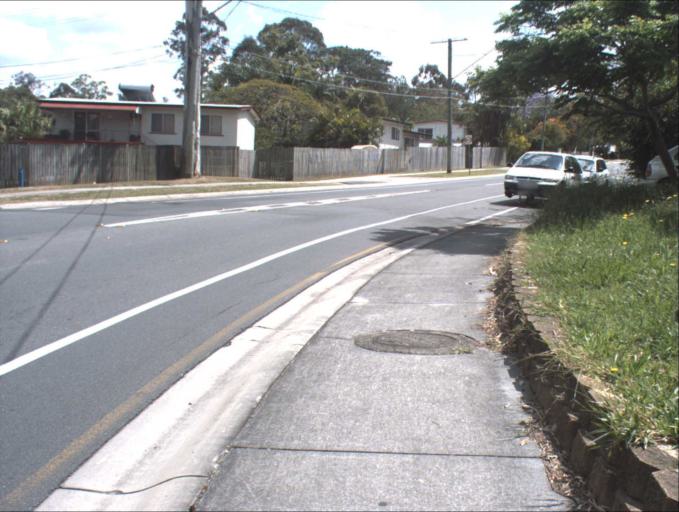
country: AU
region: Queensland
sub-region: Logan
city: Woodridge
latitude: -27.6236
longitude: 153.0986
